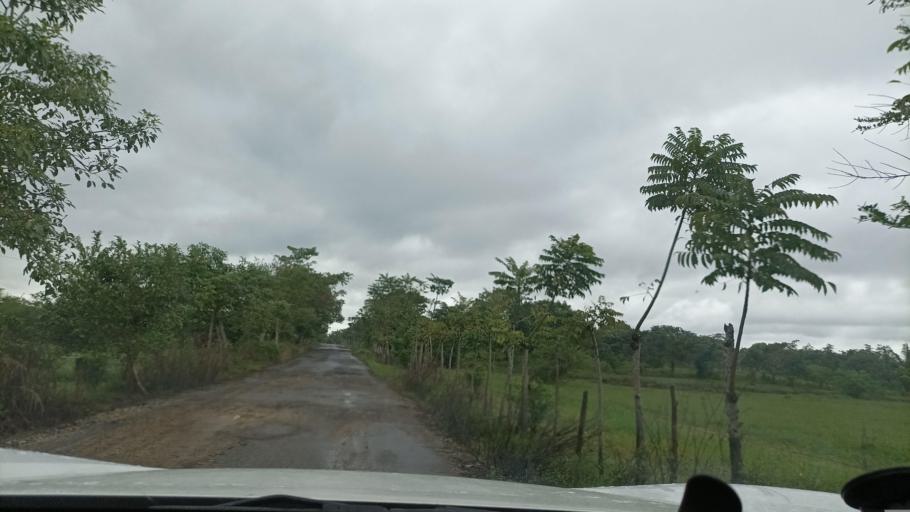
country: MX
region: Veracruz
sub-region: Moloacan
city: Cuichapa
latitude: 17.7698
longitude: -94.3884
